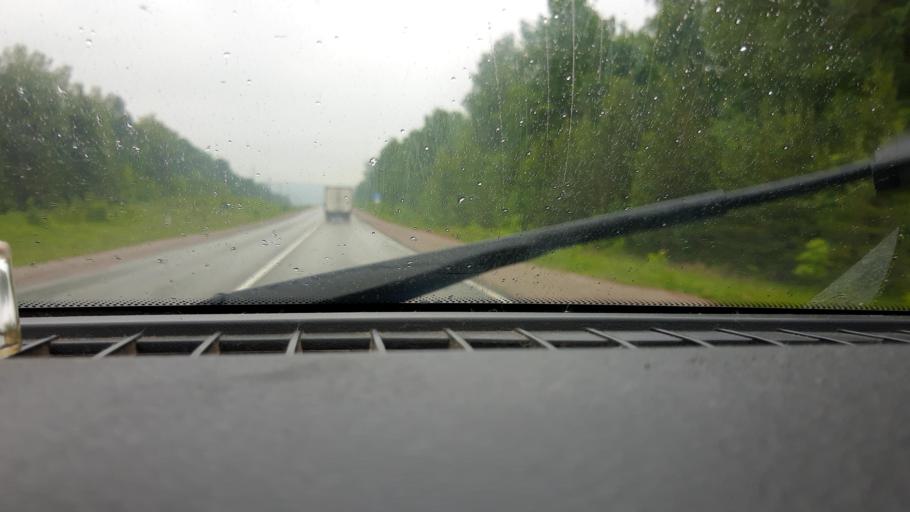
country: RU
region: Bashkortostan
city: Belebey
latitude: 54.2195
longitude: 54.0754
